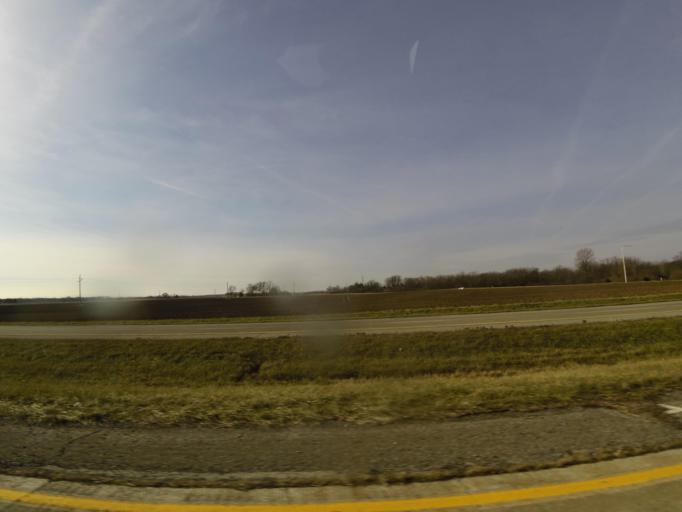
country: US
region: Illinois
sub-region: De Witt County
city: Clinton
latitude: 40.1265
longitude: -88.9655
